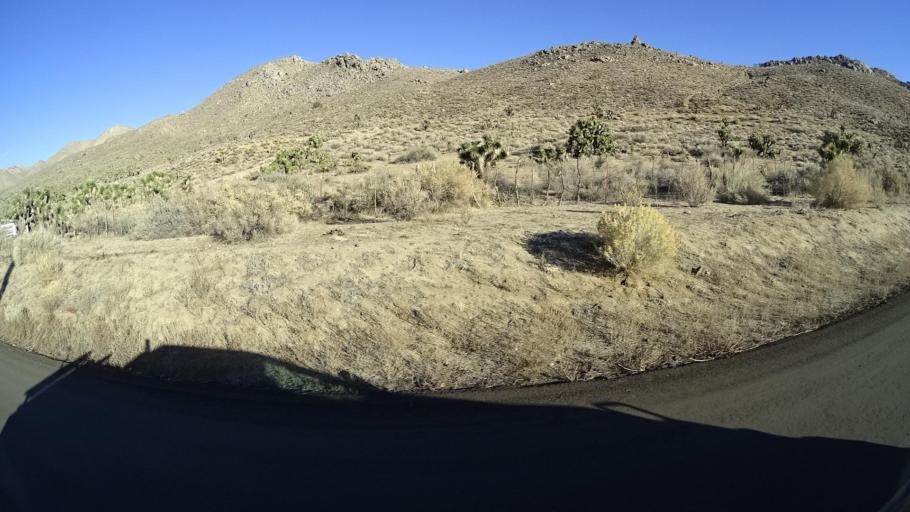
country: US
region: California
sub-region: Kern County
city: Weldon
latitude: 35.5104
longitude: -118.2027
